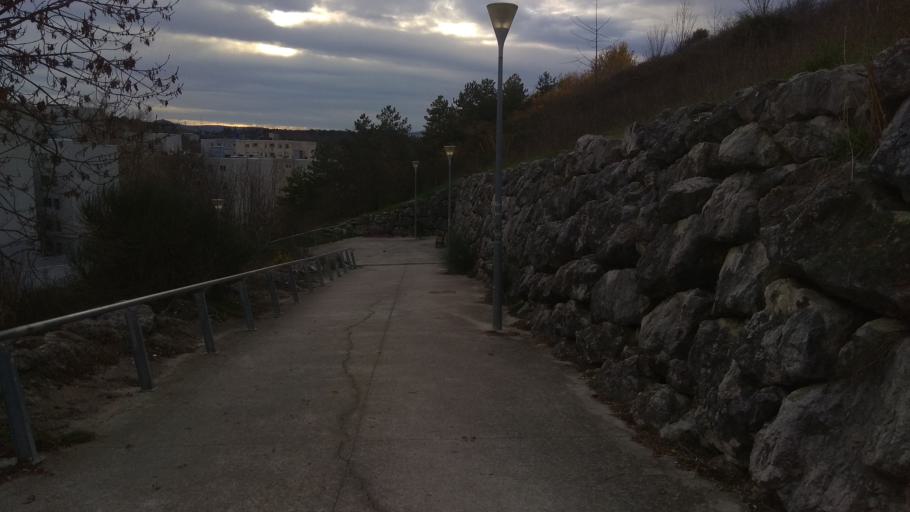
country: ES
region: Navarre
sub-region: Provincia de Navarra
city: Baranain
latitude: 42.8021
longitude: -1.6759
